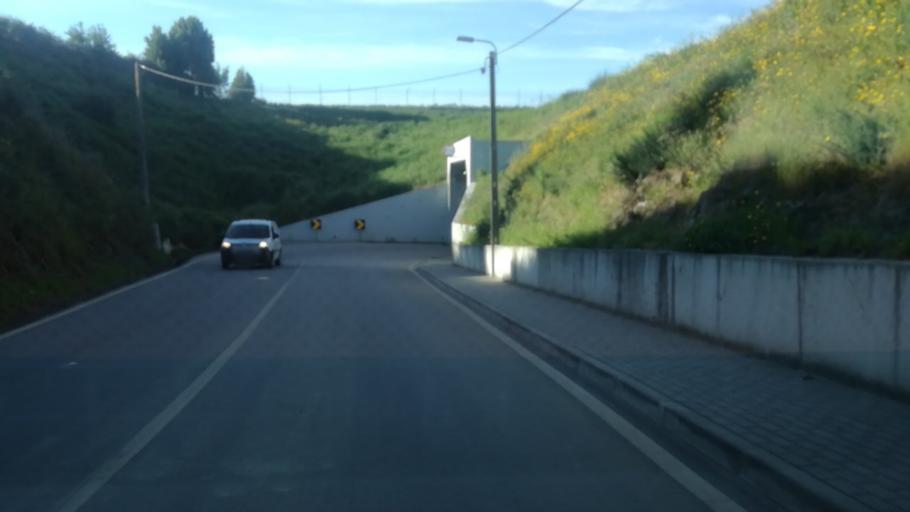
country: PT
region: Porto
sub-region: Matosinhos
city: Santa Cruz do Bispo
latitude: 41.2499
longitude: -8.6846
